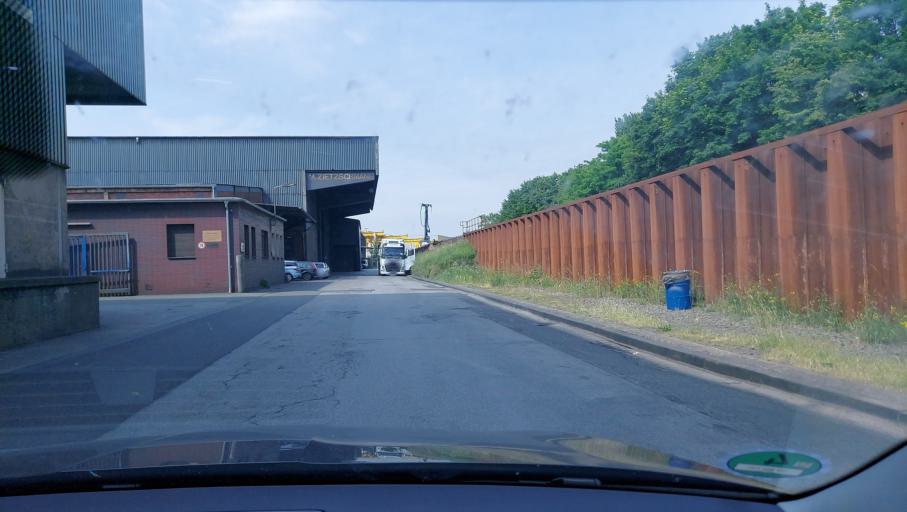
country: DE
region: North Rhine-Westphalia
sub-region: Regierungsbezirk Dusseldorf
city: Hochfeld
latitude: 51.4303
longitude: 6.7341
